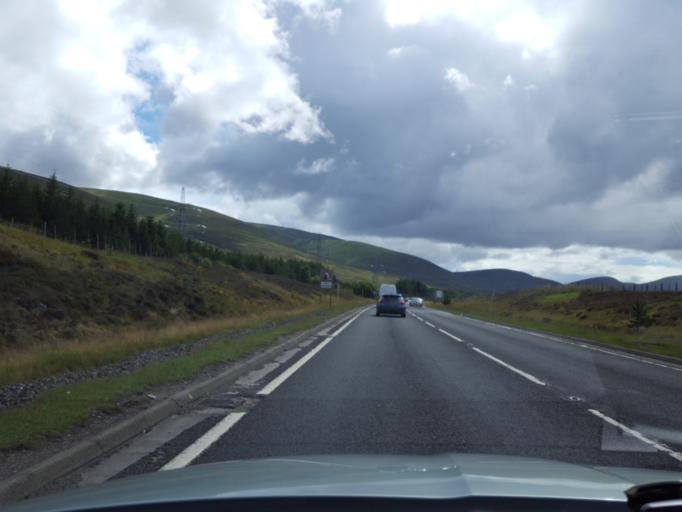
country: GB
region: Scotland
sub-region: Highland
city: Kingussie
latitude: 56.9152
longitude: -4.2356
